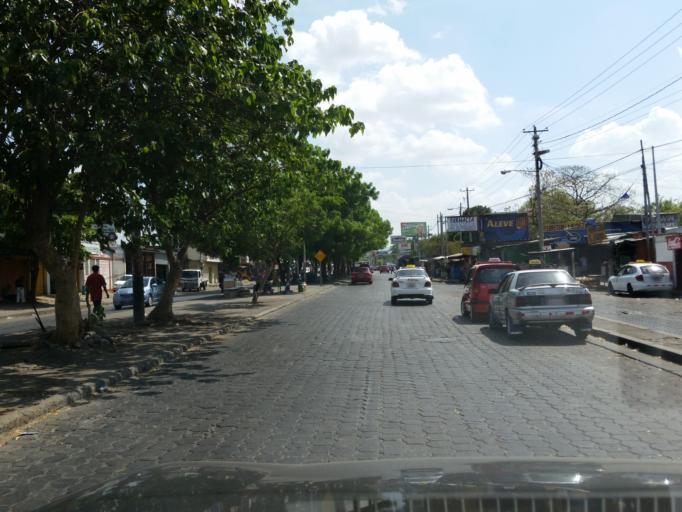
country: NI
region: Managua
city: Managua
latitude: 12.1237
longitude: -86.2423
